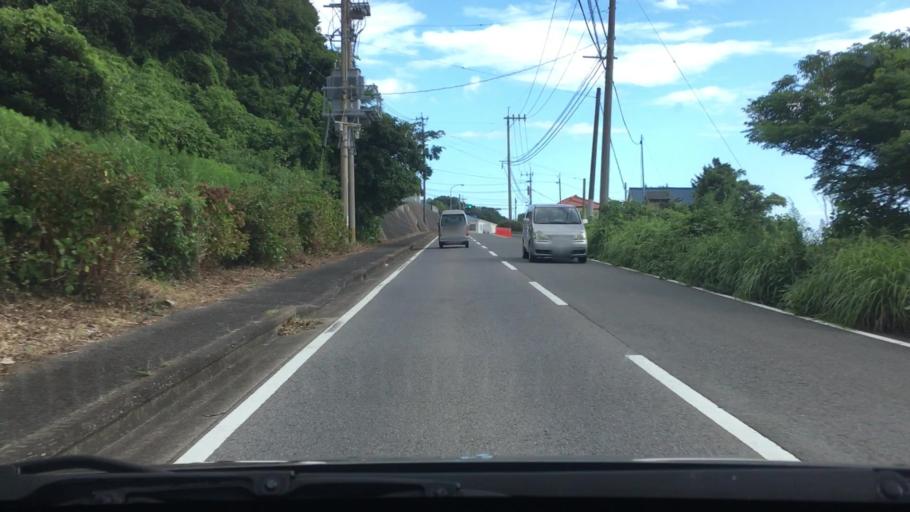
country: JP
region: Nagasaki
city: Togitsu
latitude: 32.8643
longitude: 129.6834
